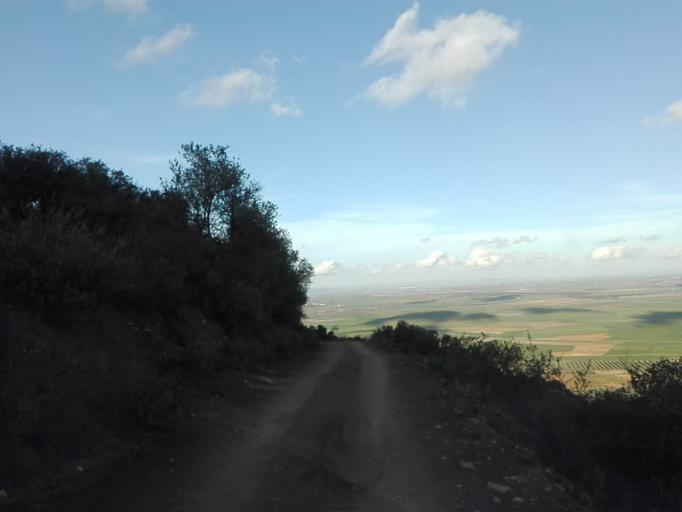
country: ES
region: Extremadura
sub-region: Provincia de Badajoz
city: Llerena
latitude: 38.2128
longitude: -5.9969
